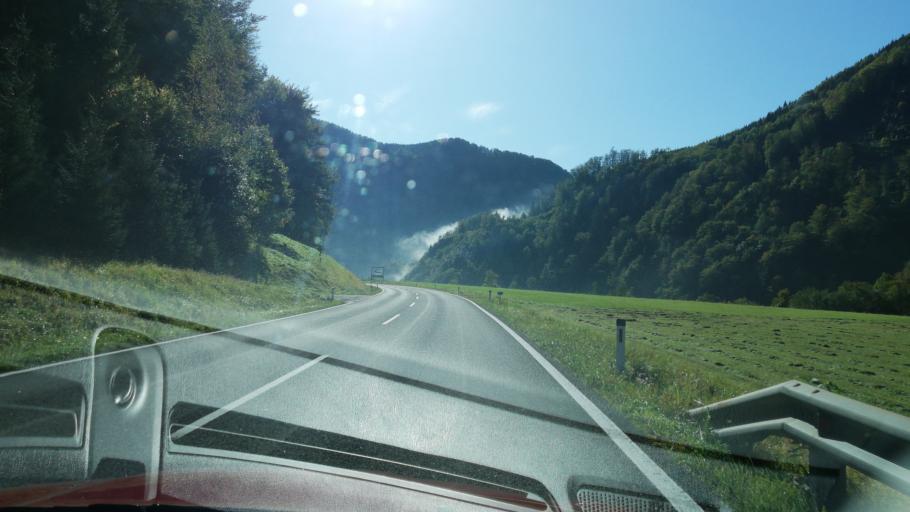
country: AT
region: Styria
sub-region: Politischer Bezirk Liezen
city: Altenmarkt bei Sankt Gallen
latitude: 47.7449
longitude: 14.6442
